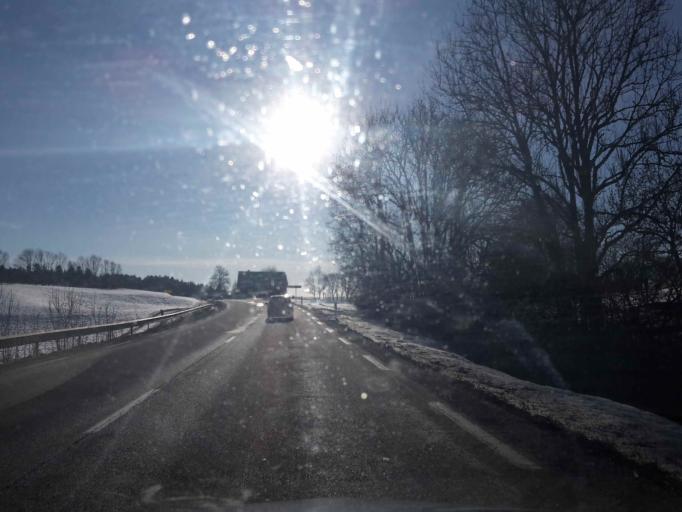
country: FR
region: Franche-Comte
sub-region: Departement du Doubs
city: Doubs
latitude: 47.0354
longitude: 6.3370
